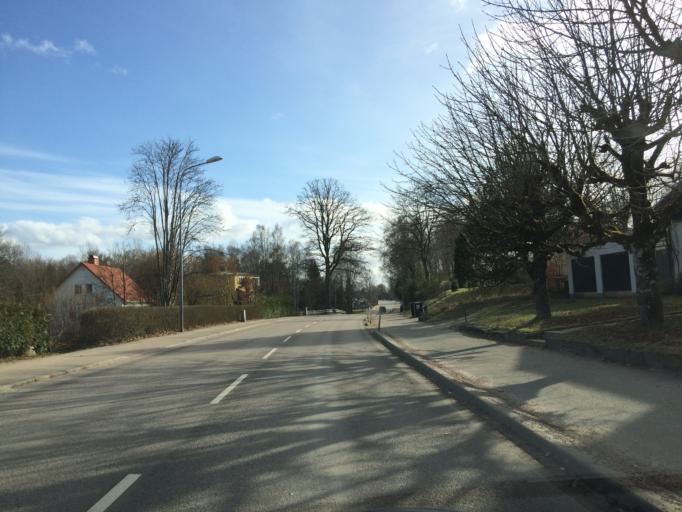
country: SE
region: Kronoberg
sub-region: Almhults Kommun
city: AElmhult
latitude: 56.5595
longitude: 14.1307
